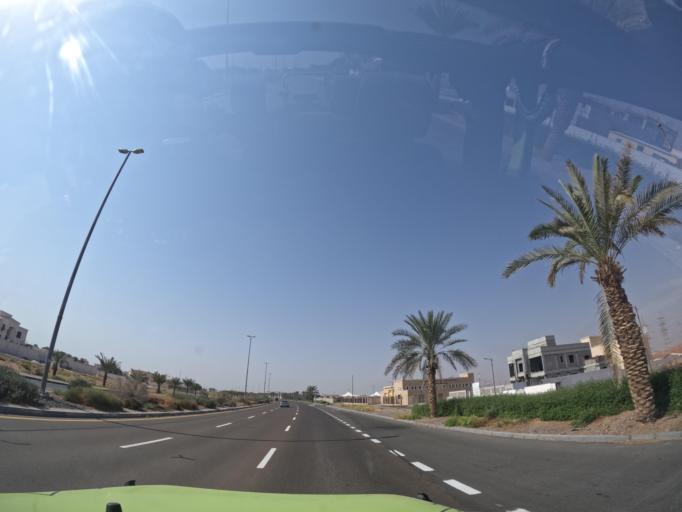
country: AE
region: Abu Dhabi
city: Al Ain
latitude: 24.2638
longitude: 55.6960
